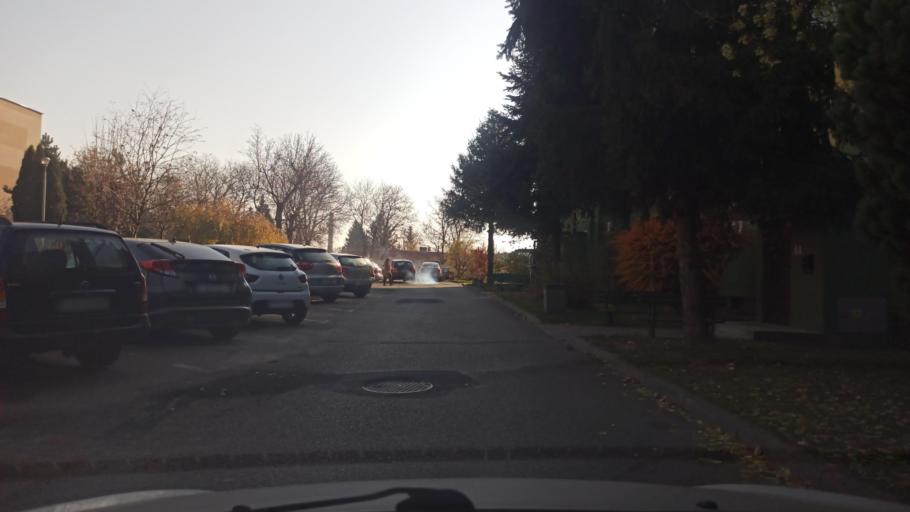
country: PL
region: Subcarpathian Voivodeship
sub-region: Powiat jaroslawski
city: Radymno
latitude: 49.9451
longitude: 22.8275
